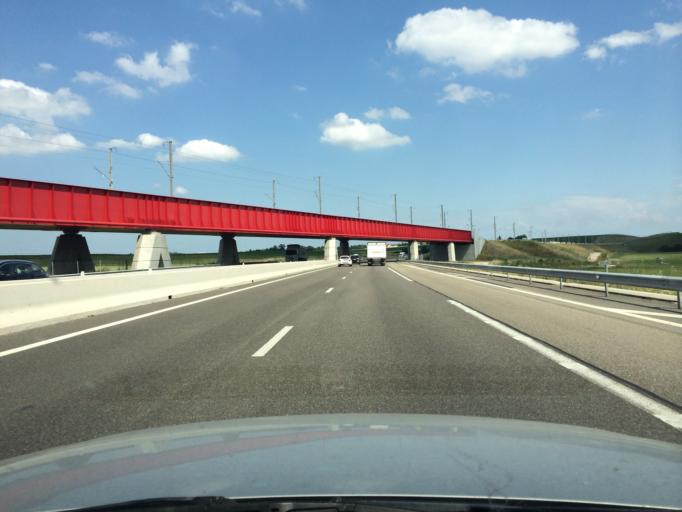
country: FR
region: Alsace
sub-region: Departement du Bas-Rhin
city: Dettwiller
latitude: 48.7733
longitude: 7.4517
